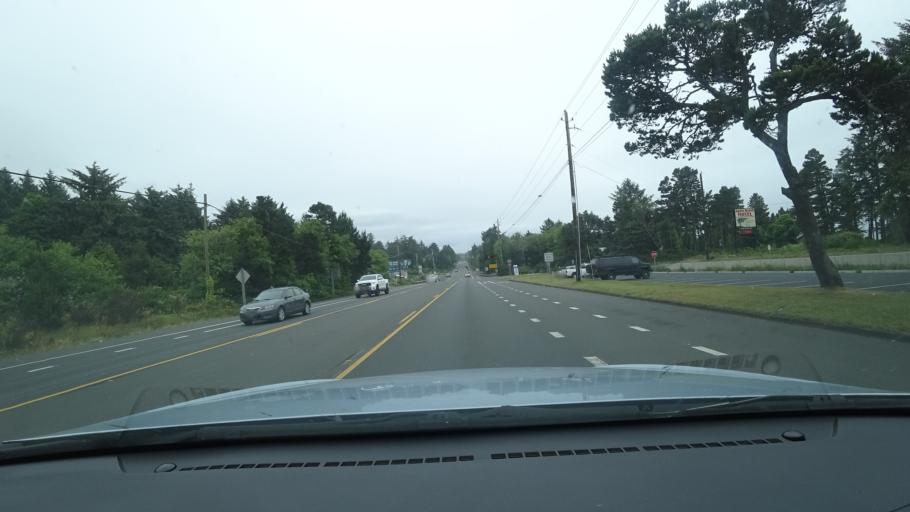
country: US
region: Oregon
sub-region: Lincoln County
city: Newport
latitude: 44.6745
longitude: -124.0594
